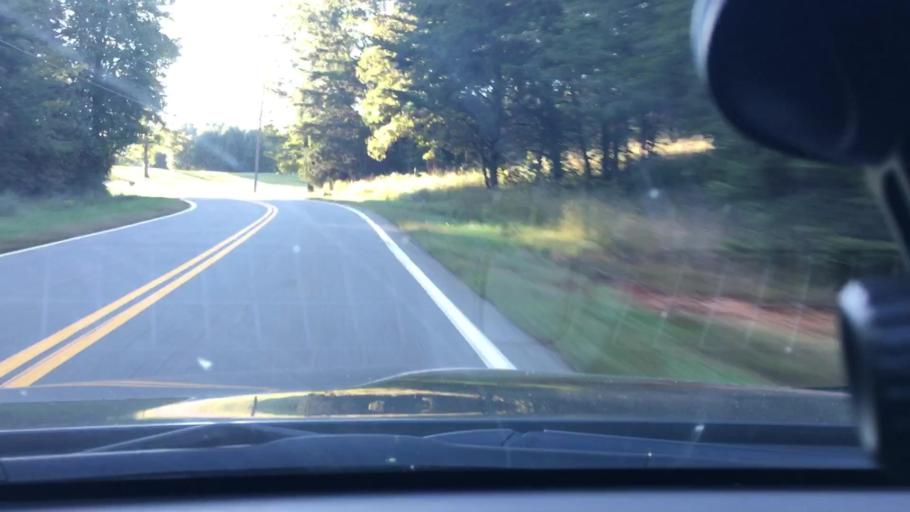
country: US
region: North Carolina
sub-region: Rutherford County
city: Rutherfordton
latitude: 35.3313
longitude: -82.0504
